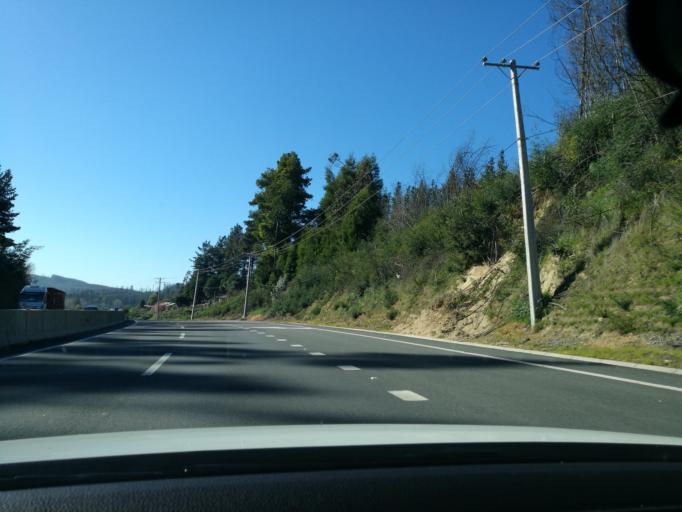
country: CL
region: Biobio
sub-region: Provincia de Concepcion
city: Chiguayante
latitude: -36.8550
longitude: -72.8950
